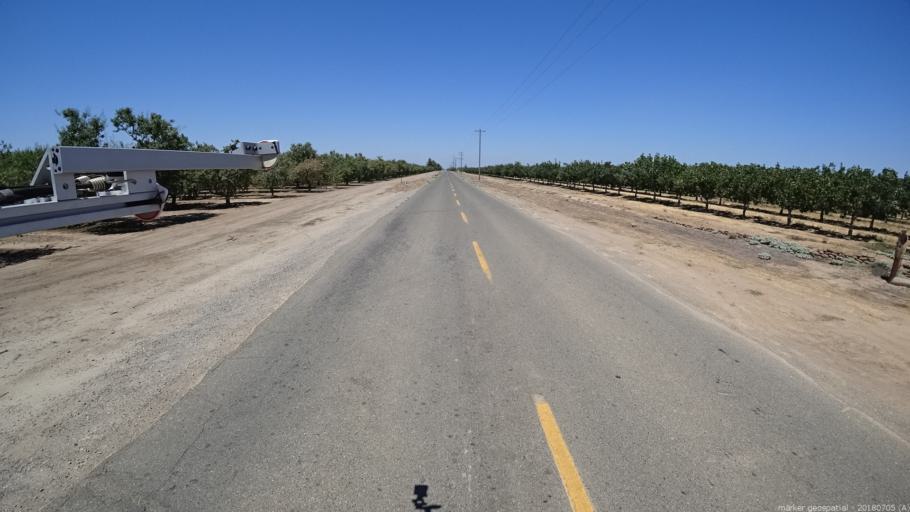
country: US
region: California
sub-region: Madera County
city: Fairmead
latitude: 37.0981
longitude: -120.1425
